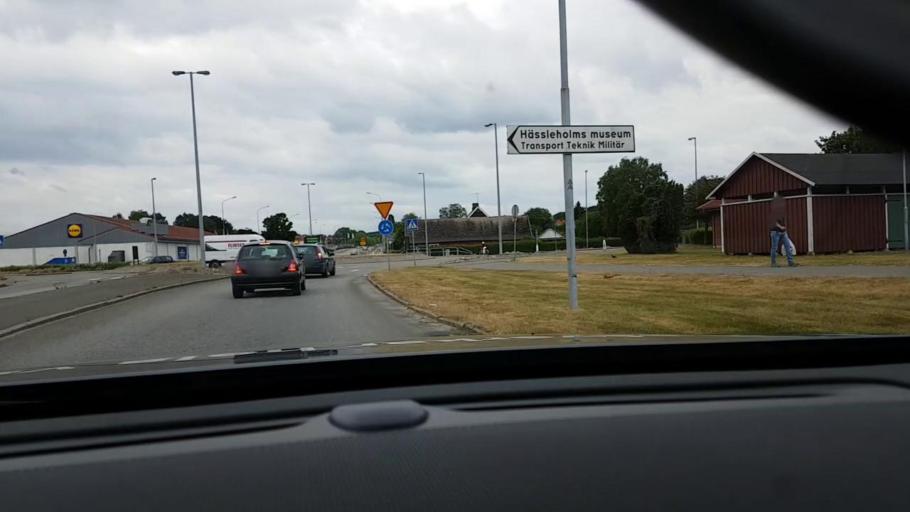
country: SE
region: Skane
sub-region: Hassleholms Kommun
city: Hassleholm
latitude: 56.1664
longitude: 13.7876
